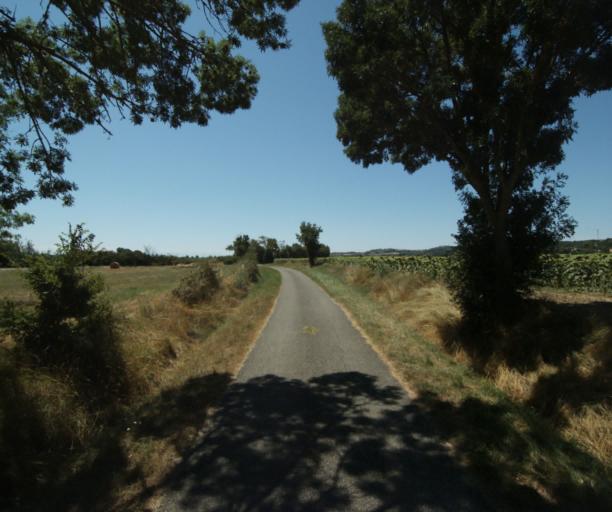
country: FR
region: Midi-Pyrenees
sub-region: Departement de la Haute-Garonne
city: Saint-Felix-Lauragais
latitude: 43.4603
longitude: 1.9369
